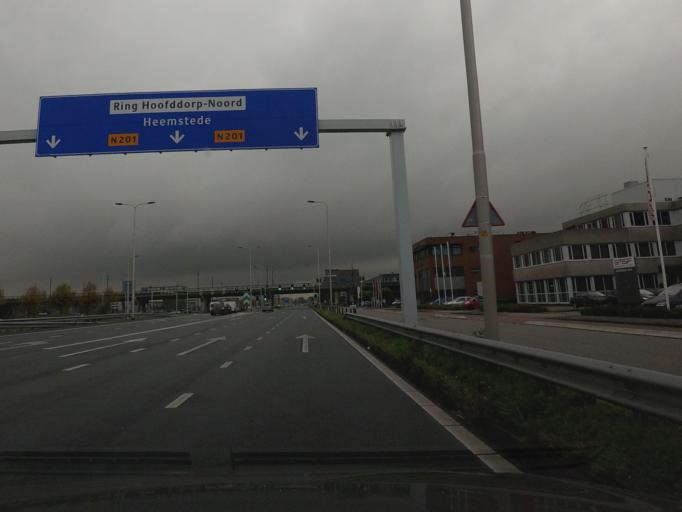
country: NL
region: North Holland
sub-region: Gemeente Haarlemmermeer
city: Hoofddorp
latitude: 52.2896
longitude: 4.7223
